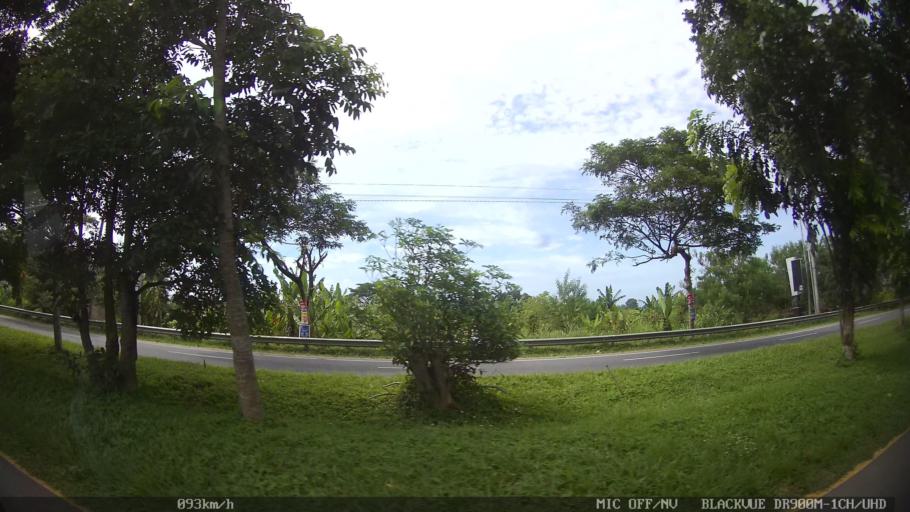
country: ID
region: North Sumatra
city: Percut
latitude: 3.5991
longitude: 98.8276
